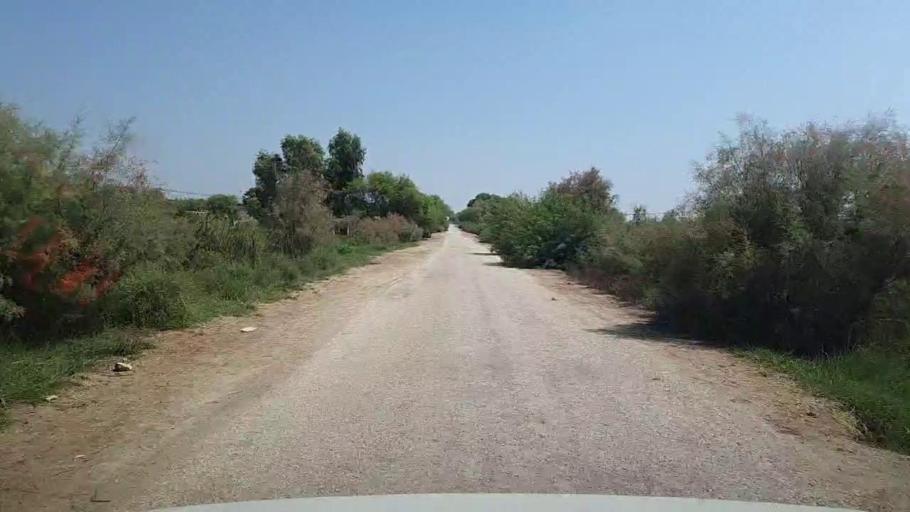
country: PK
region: Sindh
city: Kandhkot
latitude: 28.2900
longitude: 69.3524
